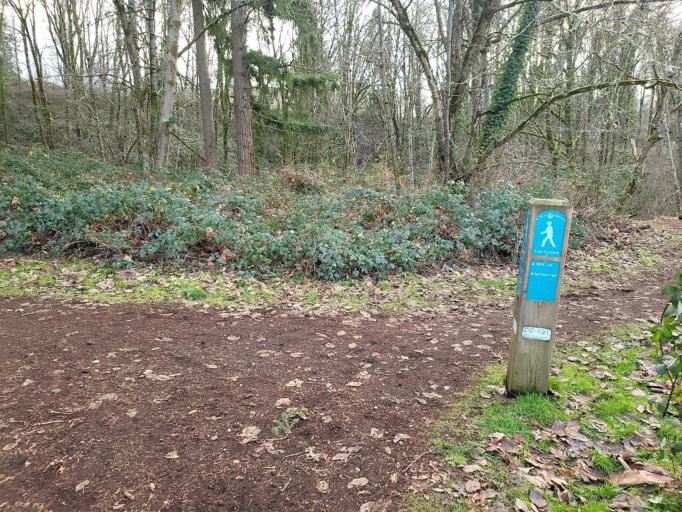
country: US
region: Washington
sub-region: King County
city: Newcastle
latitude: 47.5427
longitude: -122.1558
